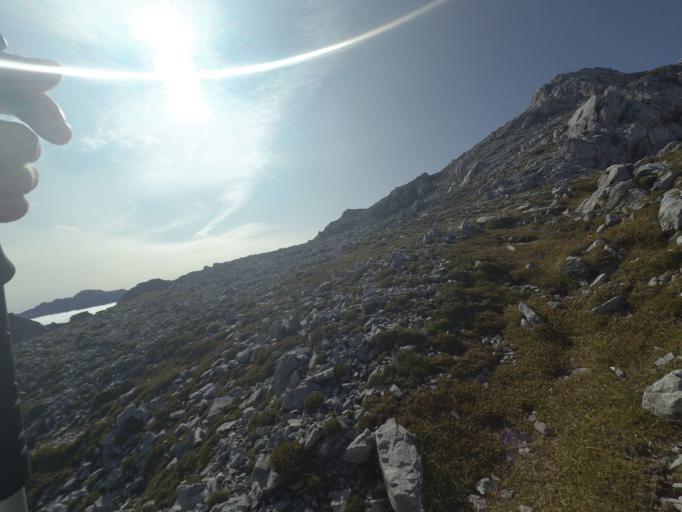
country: AT
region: Salzburg
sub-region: Politischer Bezirk Sankt Johann im Pongau
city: Kleinarl
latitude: 47.2167
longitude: 13.4029
